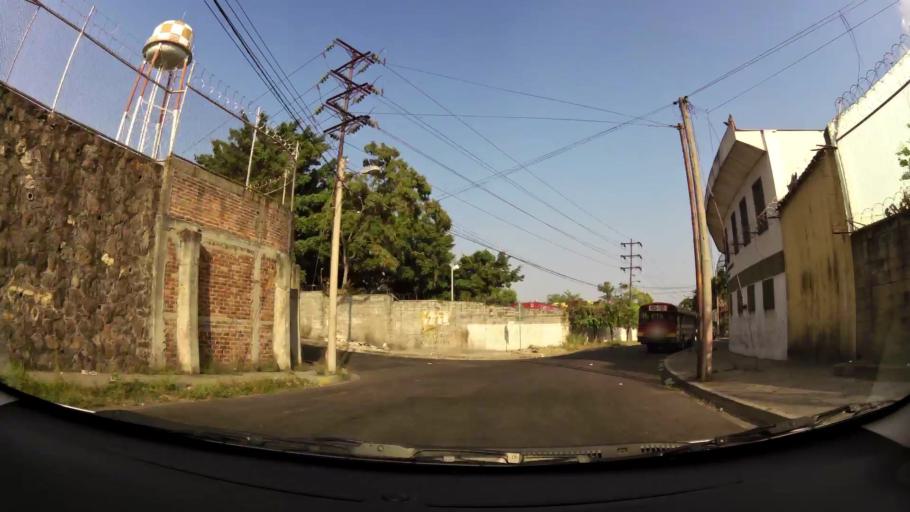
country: SV
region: San Salvador
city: San Salvador
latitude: 13.6979
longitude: -89.1809
